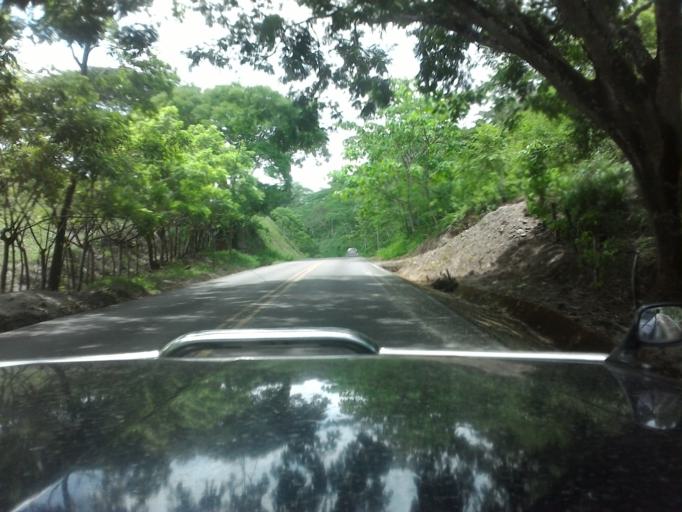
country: CR
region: Puntarenas
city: Miramar
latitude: 10.1836
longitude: -84.8373
